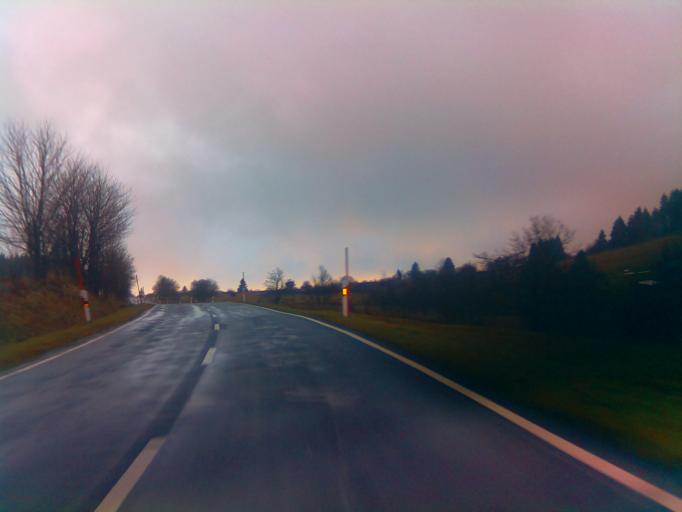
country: DE
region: Bavaria
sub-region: Regierungsbezirk Unterfranken
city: Bischofsheim an der Rhon
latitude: 50.4718
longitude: 10.0125
